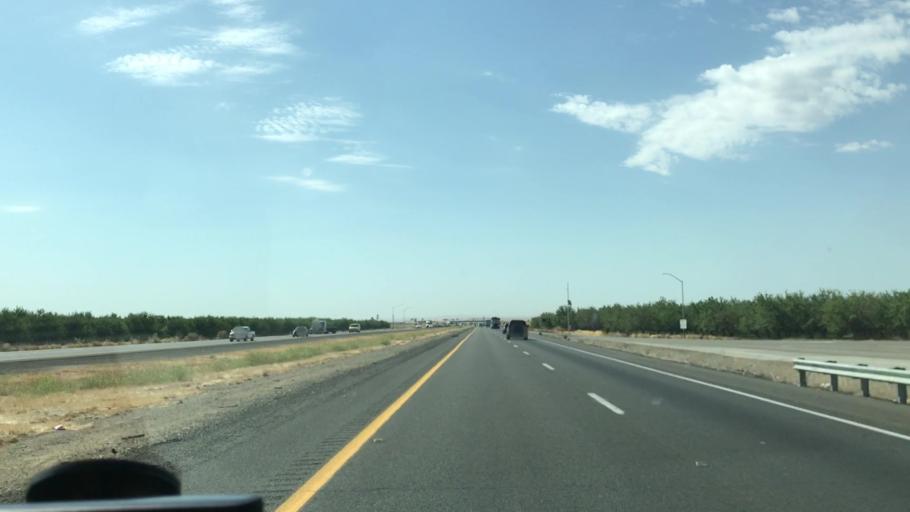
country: US
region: California
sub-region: Merced County
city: Gustine
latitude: 37.1265
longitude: -121.0302
